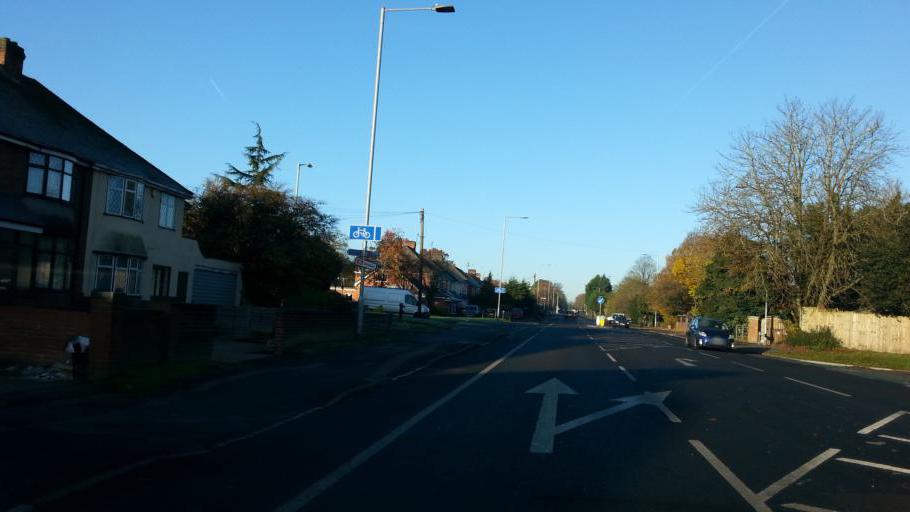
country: GB
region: England
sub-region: Wokingham
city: Earley
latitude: 51.4396
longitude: -0.9178
